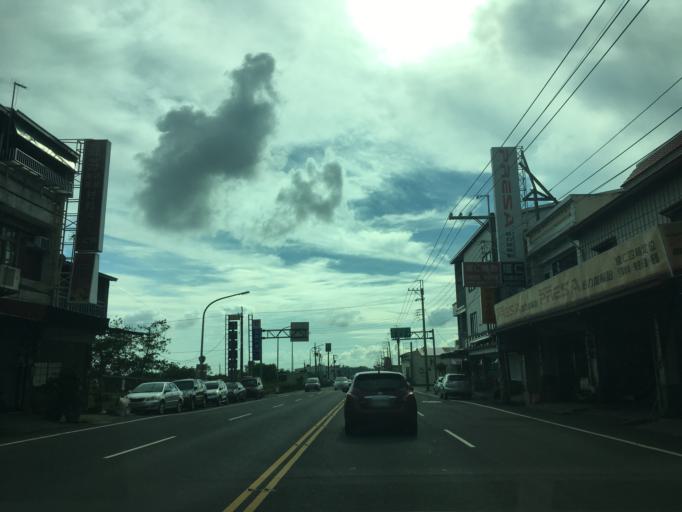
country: TW
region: Taiwan
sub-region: Chiayi
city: Jiayi Shi
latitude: 23.4419
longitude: 120.5247
